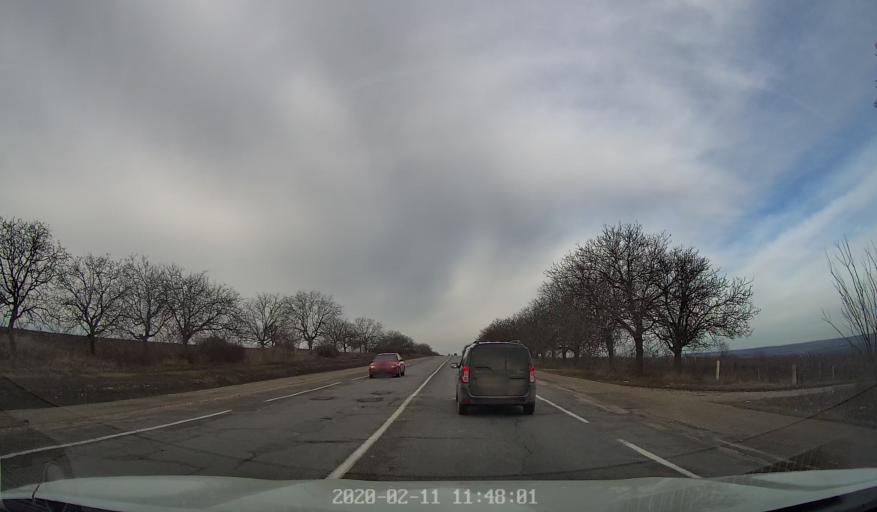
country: MD
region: Balti
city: Balti
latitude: 47.8342
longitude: 27.8084
